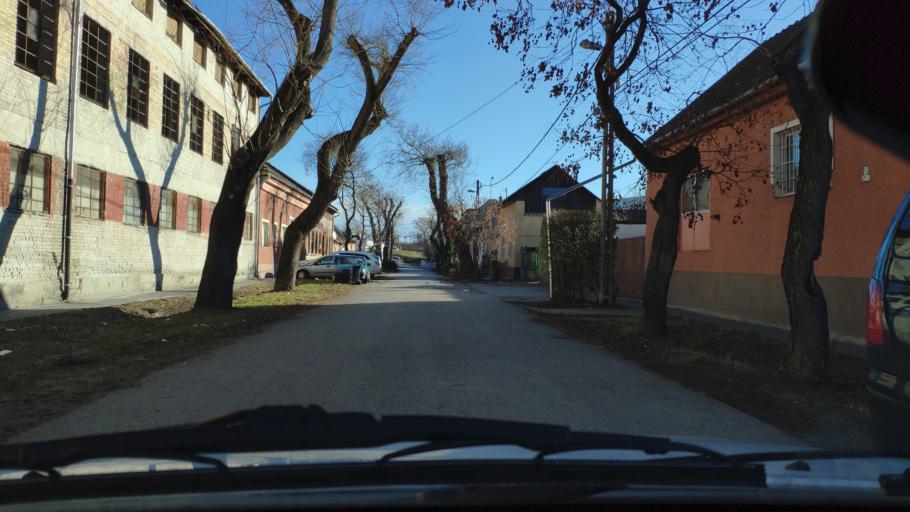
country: HU
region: Budapest
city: Budapest XXI. keruelet
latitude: 47.4357
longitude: 19.0810
